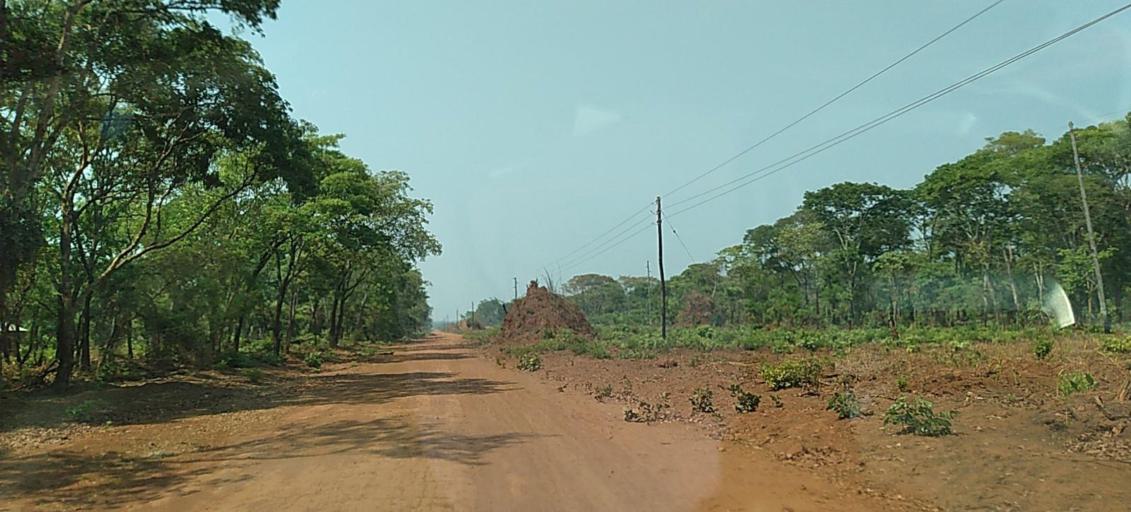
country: ZM
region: Copperbelt
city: Kalulushi
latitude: -13.0764
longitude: 27.4126
